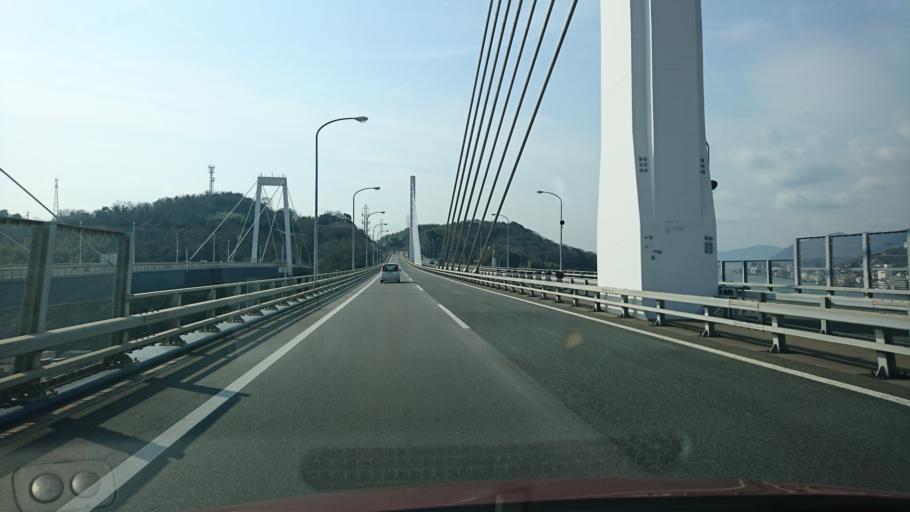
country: JP
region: Hiroshima
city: Onomichi
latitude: 34.4108
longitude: 133.2172
